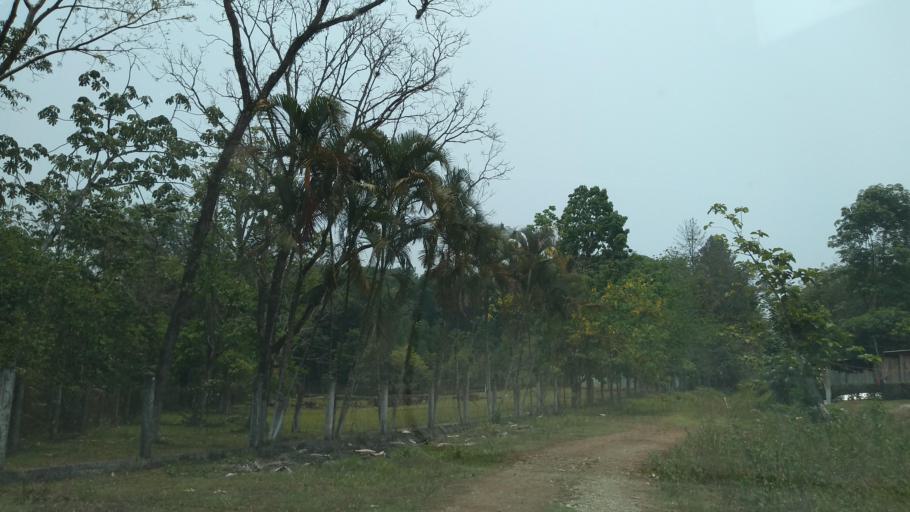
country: MX
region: Veracruz
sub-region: Tezonapa
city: Laguna Chica (Pueblo Nuevo)
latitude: 18.5126
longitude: -96.7615
